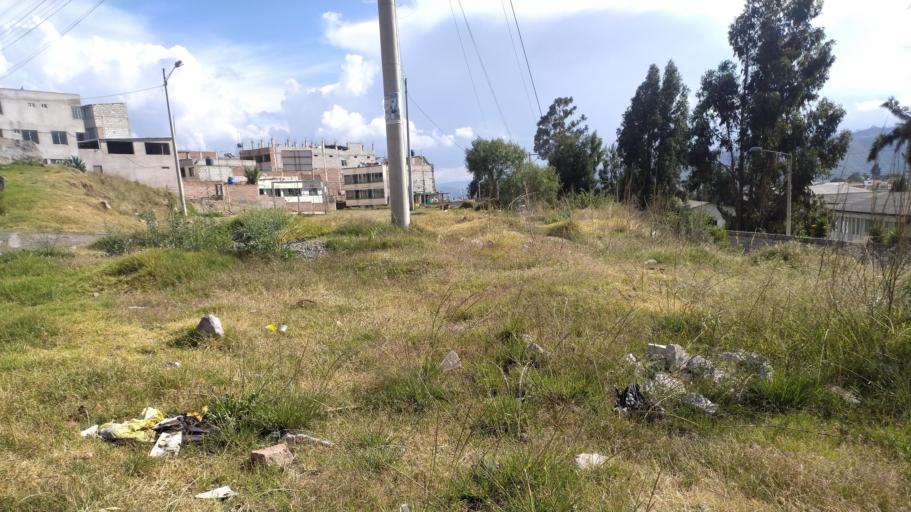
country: EC
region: Chimborazo
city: Riobamba
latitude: -1.6591
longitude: -78.6497
